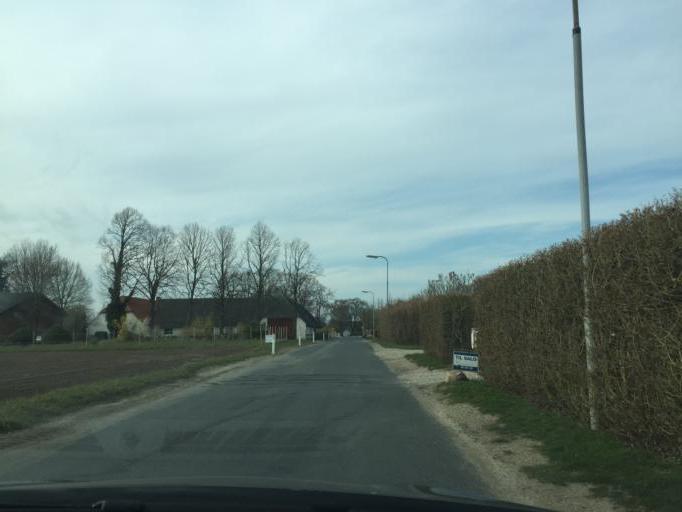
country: DK
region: South Denmark
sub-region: Faaborg-Midtfyn Kommune
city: Arslev
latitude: 55.3327
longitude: 10.5116
